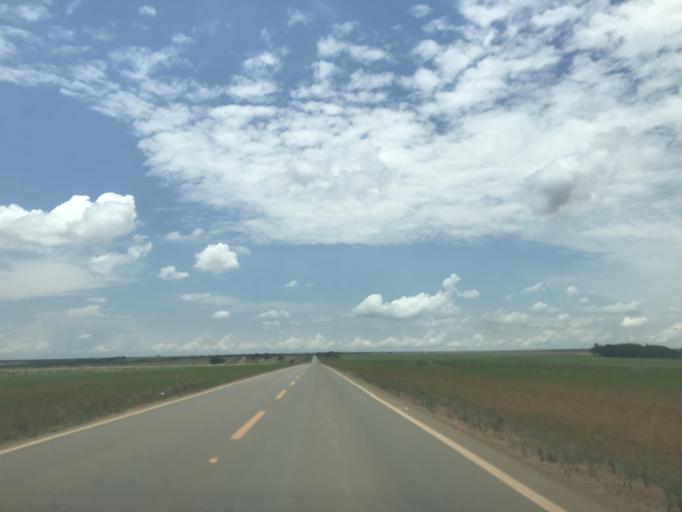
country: BR
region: Goias
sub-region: Luziania
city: Luziania
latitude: -16.4997
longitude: -48.2078
